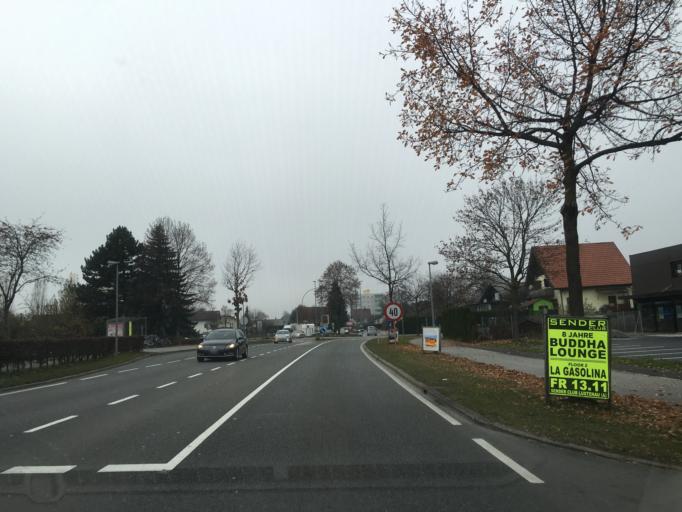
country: AT
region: Vorarlberg
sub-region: Politischer Bezirk Dornbirn
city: Lustenau
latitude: 47.4180
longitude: 9.6672
